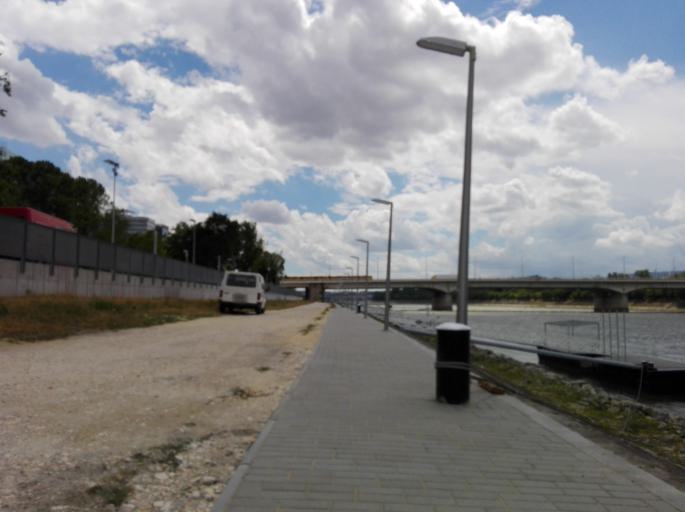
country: HU
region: Budapest
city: Budapest III. keruelet
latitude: 47.5393
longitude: 19.0590
